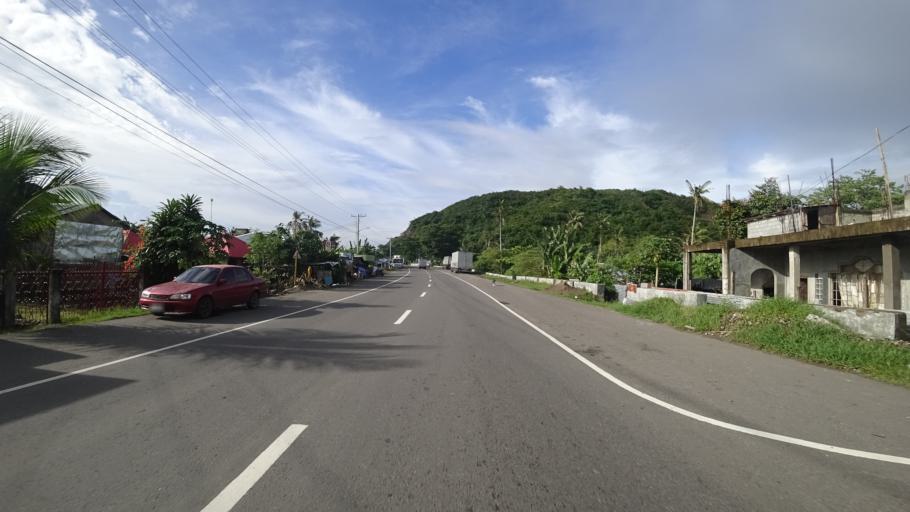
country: PH
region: Eastern Visayas
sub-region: Province of Leyte
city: Tolosa
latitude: 11.0990
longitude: 125.0193
